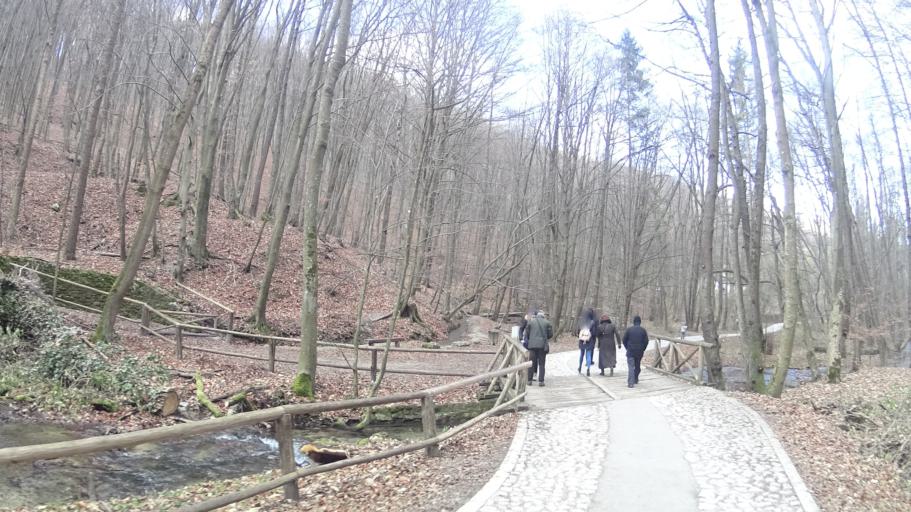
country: HU
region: Heves
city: Szilvasvarad
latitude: 48.0791
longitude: 20.4068
